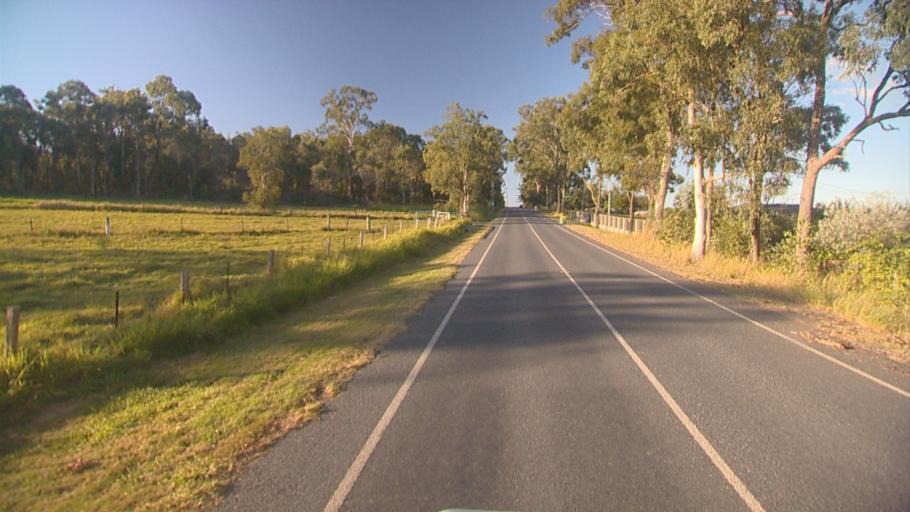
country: AU
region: Queensland
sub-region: Logan
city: Logan Reserve
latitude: -27.7210
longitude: 153.1096
